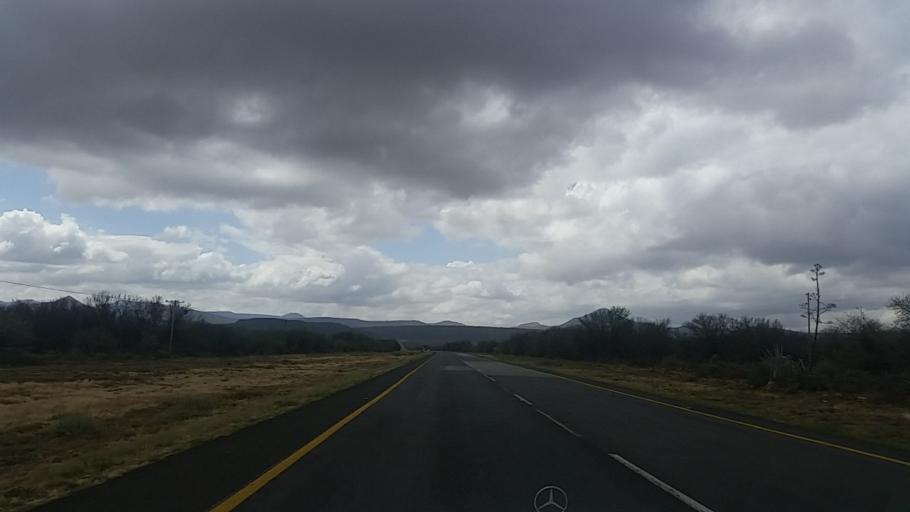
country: ZA
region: Eastern Cape
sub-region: Cacadu District Municipality
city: Graaff-Reinet
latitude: -32.1807
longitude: 24.5628
